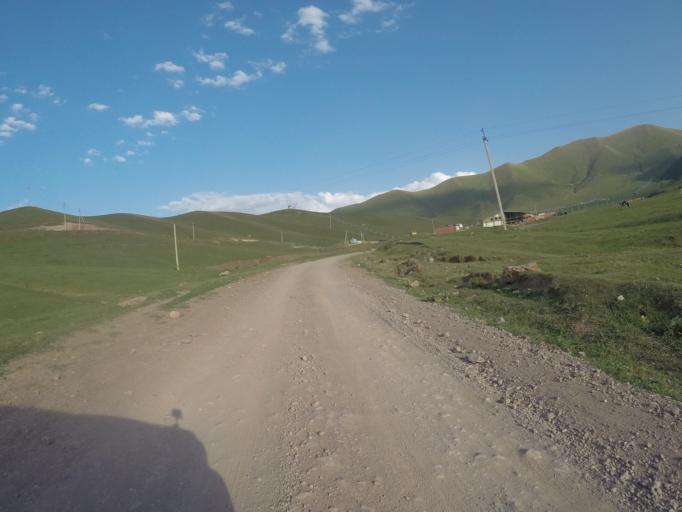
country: KG
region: Chuy
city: Bishkek
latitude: 42.6416
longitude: 74.6262
